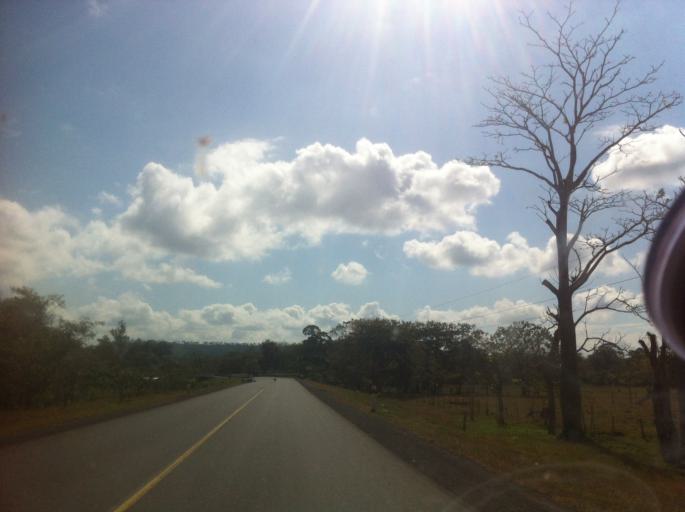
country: NI
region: Rio San Juan
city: San Carlos
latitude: 11.2490
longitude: -84.7008
